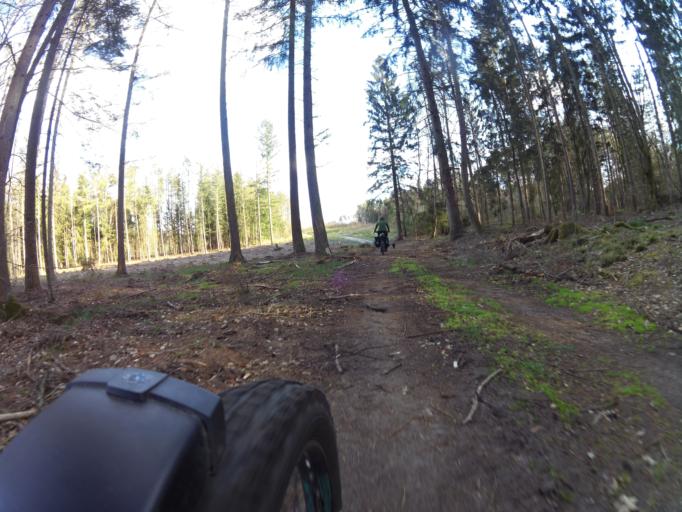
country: PL
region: West Pomeranian Voivodeship
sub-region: Powiat gryficki
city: Ploty
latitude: 53.7615
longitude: 15.2664
